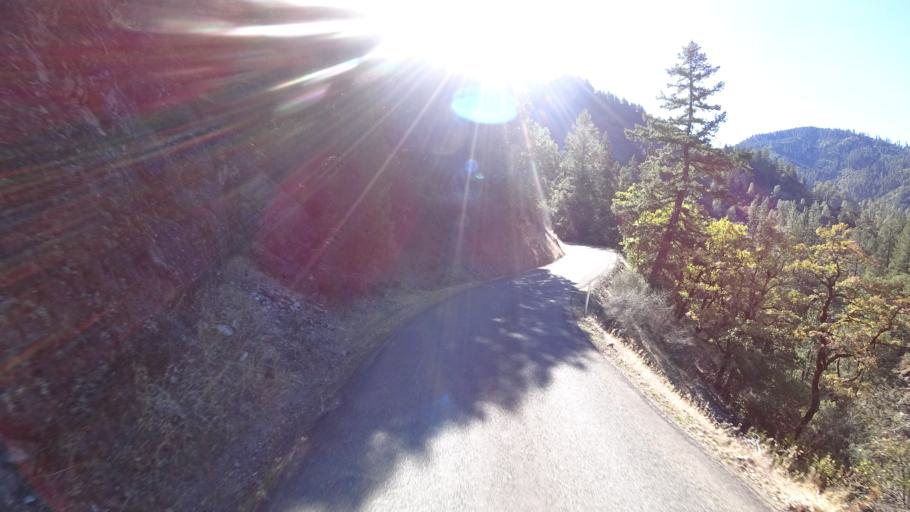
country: US
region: California
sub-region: Humboldt County
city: Willow Creek
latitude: 41.1606
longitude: -123.2078
